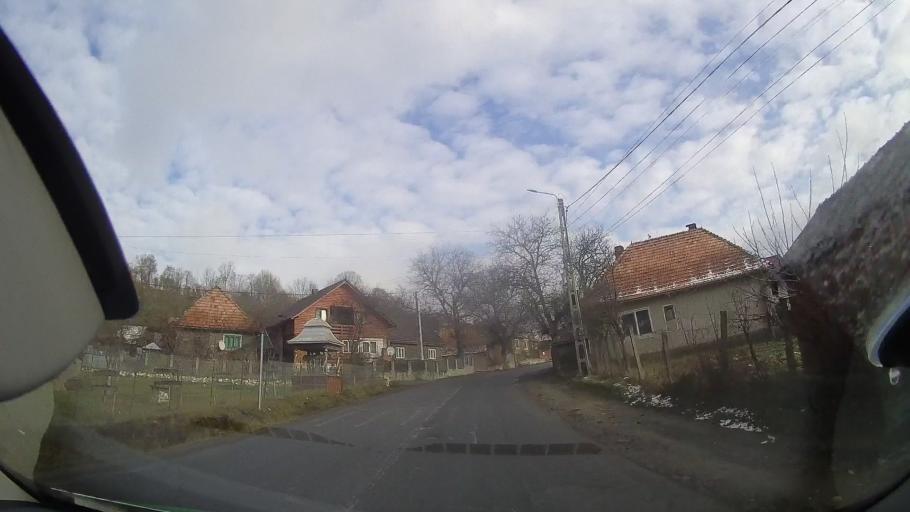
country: RO
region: Alba
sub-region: Comuna Lupsa
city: Lupsa
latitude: 46.3787
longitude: 23.2223
